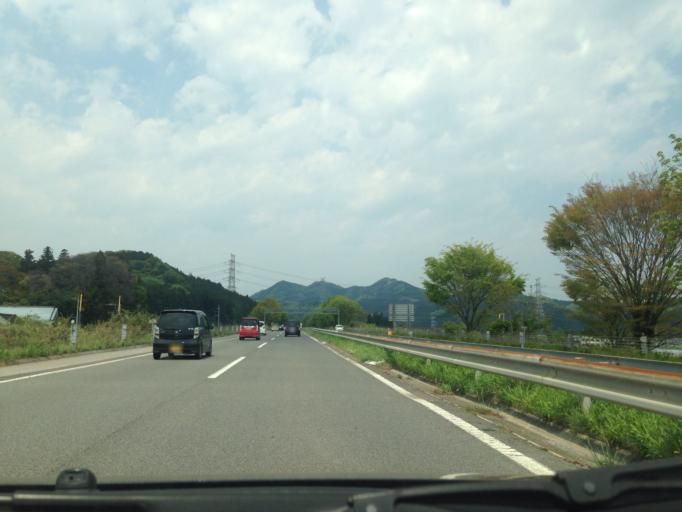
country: JP
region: Tochigi
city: Utsunomiya-shi
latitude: 36.6542
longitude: 139.8362
